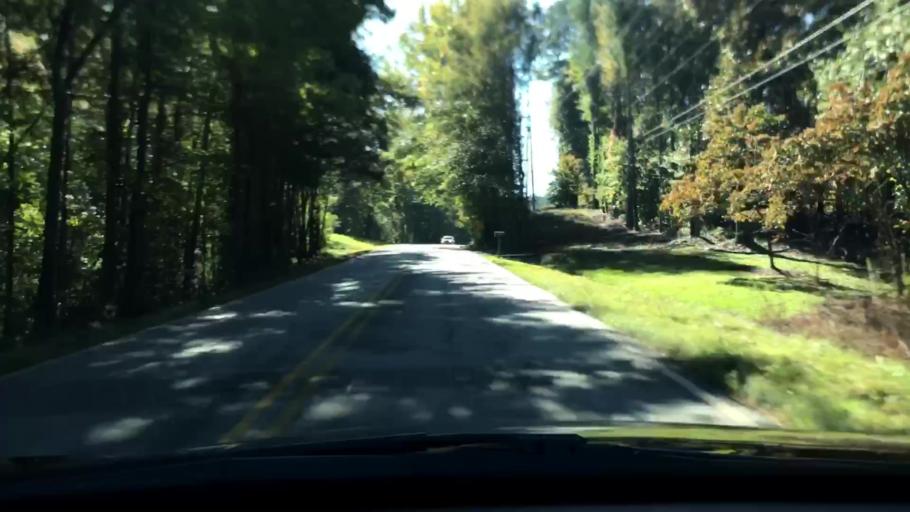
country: US
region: Georgia
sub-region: Carroll County
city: Villa Rica
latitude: 33.7428
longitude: -84.9071
